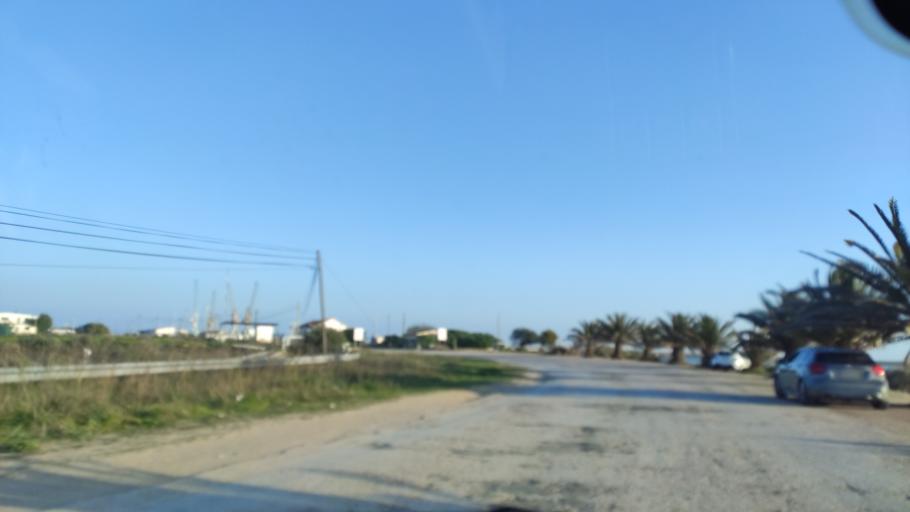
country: PT
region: Faro
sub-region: Faro
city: Faro
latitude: 37.0051
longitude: -7.9237
